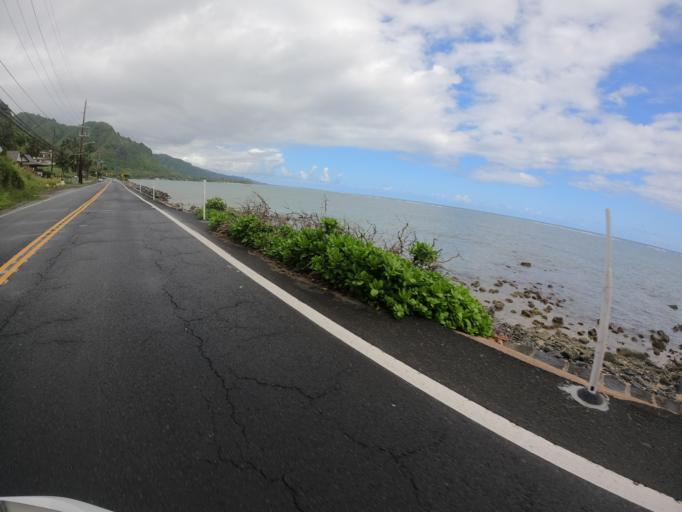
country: US
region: Hawaii
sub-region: Honolulu County
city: Ka'a'awa
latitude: 21.5597
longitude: -157.8616
